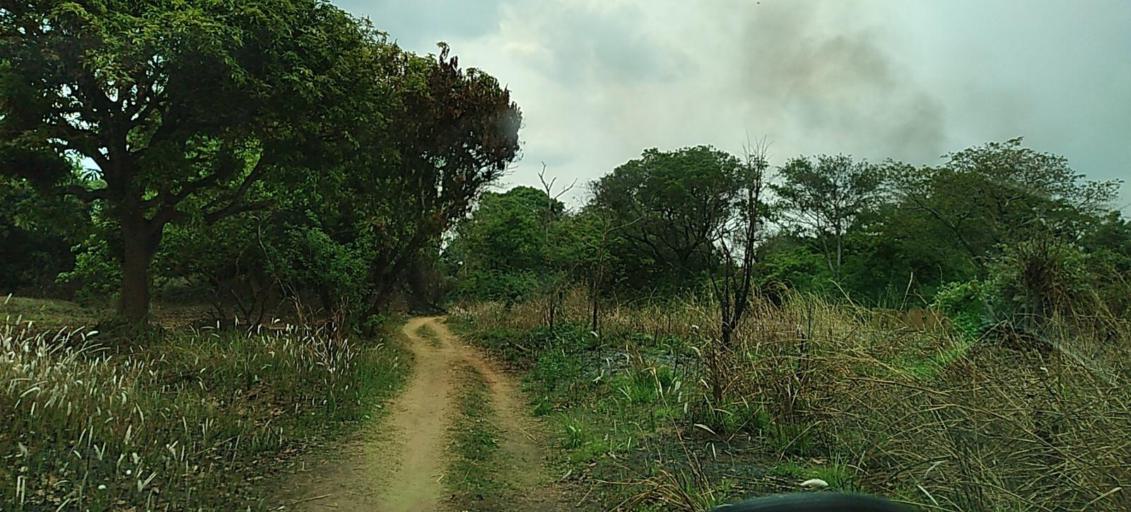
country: ZM
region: North-Western
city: Solwezi
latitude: -12.7952
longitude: 26.5296
